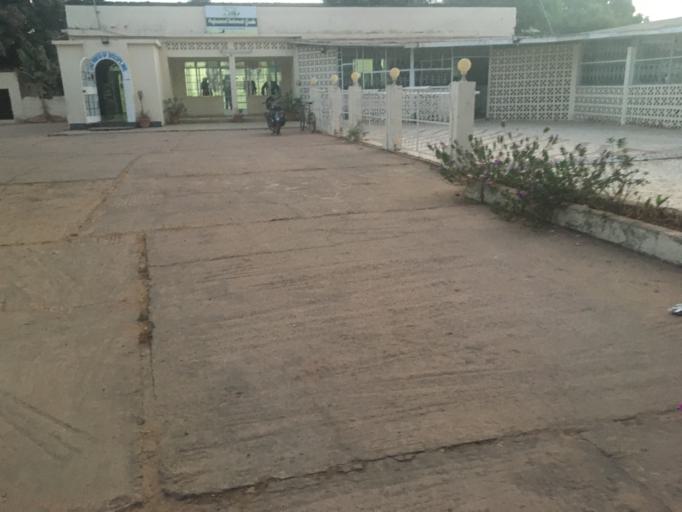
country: GM
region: Banjul
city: Bakau
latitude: 13.4696
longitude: -16.6931
